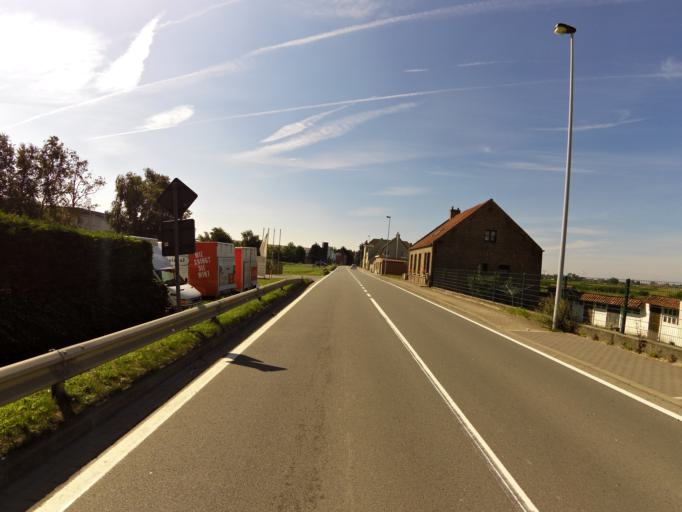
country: BE
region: Flanders
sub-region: Provincie West-Vlaanderen
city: Oudenburg
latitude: 51.2009
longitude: 3.0069
